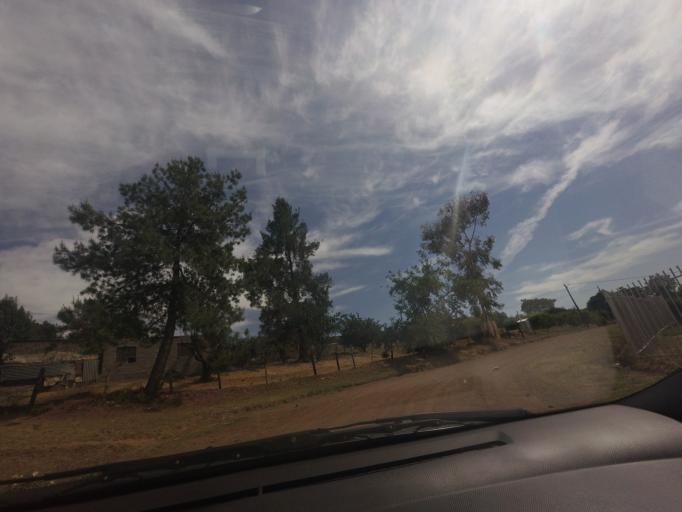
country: LS
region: Berea
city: Teyateyaneng
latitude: -29.1523
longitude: 27.7532
